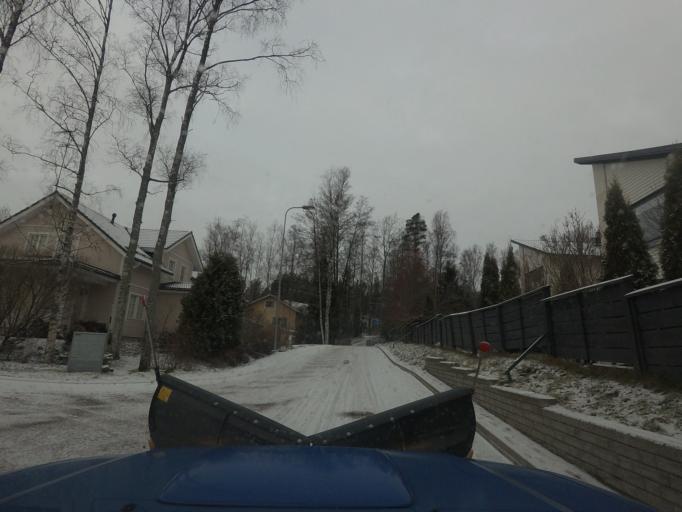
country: FI
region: Uusimaa
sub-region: Helsinki
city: Kilo
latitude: 60.2424
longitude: 24.7755
